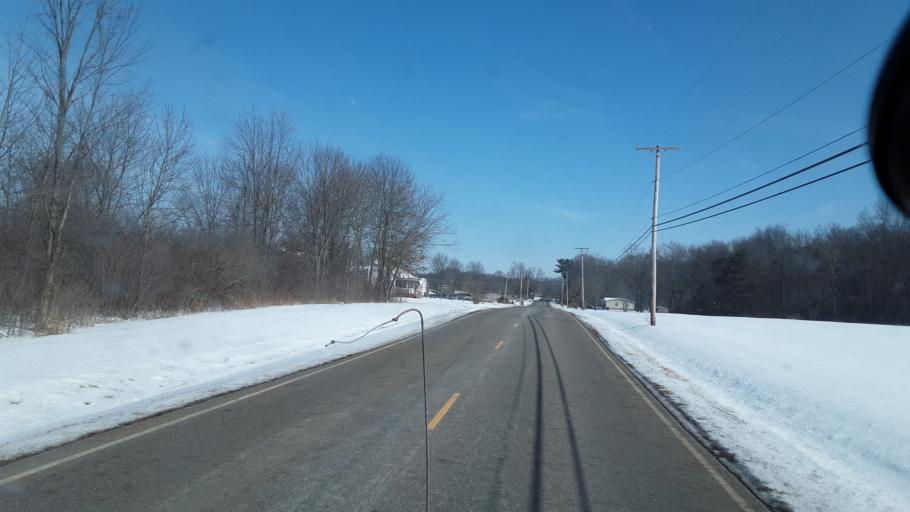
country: US
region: Ohio
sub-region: Stark County
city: Alliance
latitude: 40.9623
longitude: -81.1018
